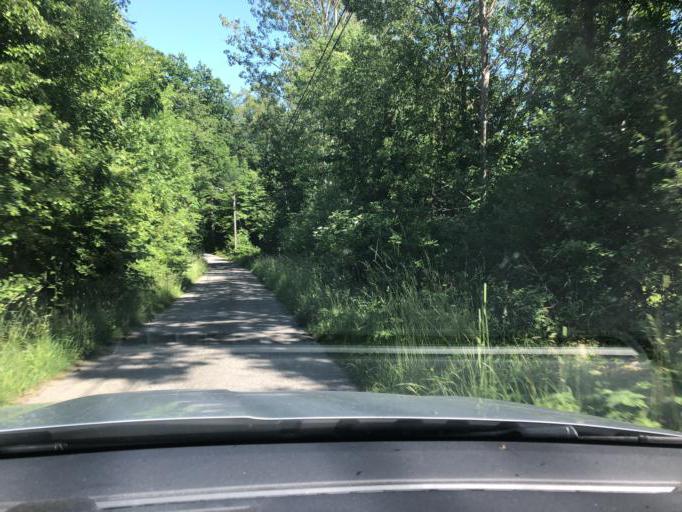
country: SE
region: Blekinge
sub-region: Karlshamns Kommun
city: Morrum
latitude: 56.1903
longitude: 14.6914
